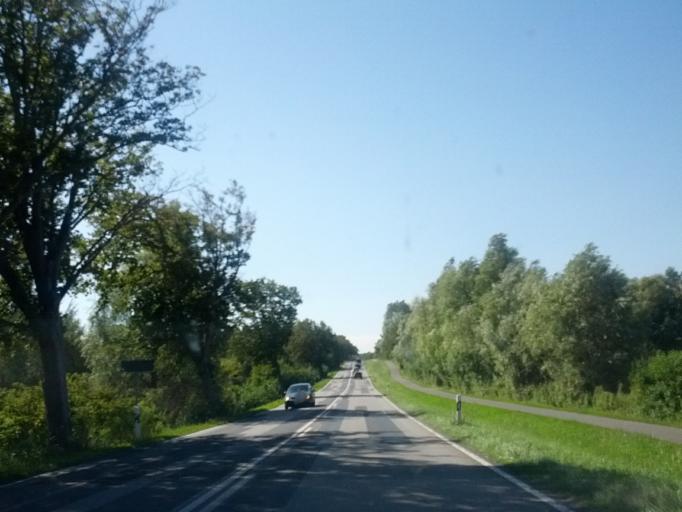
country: DE
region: Mecklenburg-Vorpommern
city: Sagard
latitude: 54.5030
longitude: 13.5289
